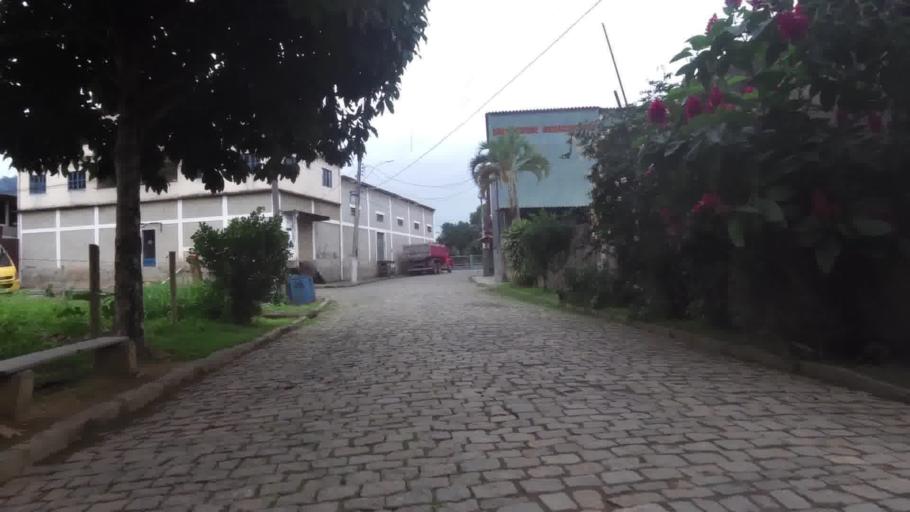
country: BR
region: Espirito Santo
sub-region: Iconha
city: Iconha
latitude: -20.7954
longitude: -40.8131
